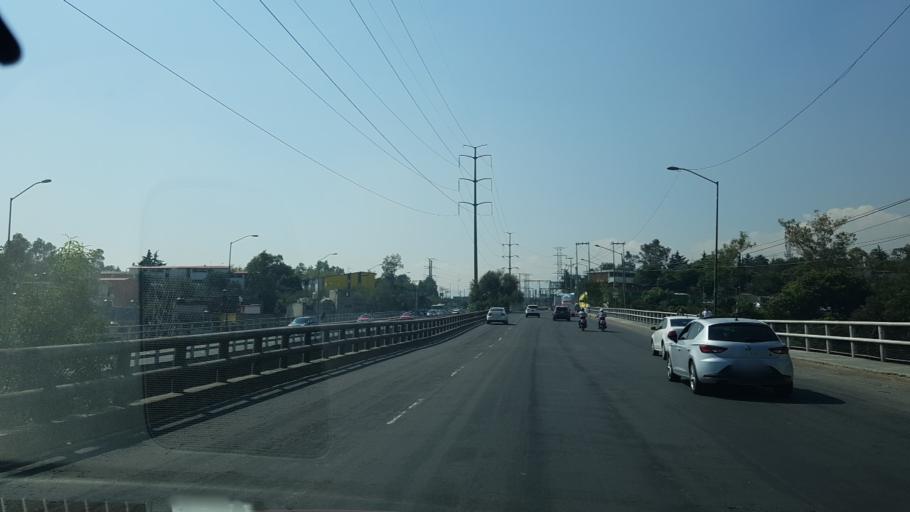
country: MX
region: Mexico City
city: Alvaro Obregon
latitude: 19.3704
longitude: -99.2041
